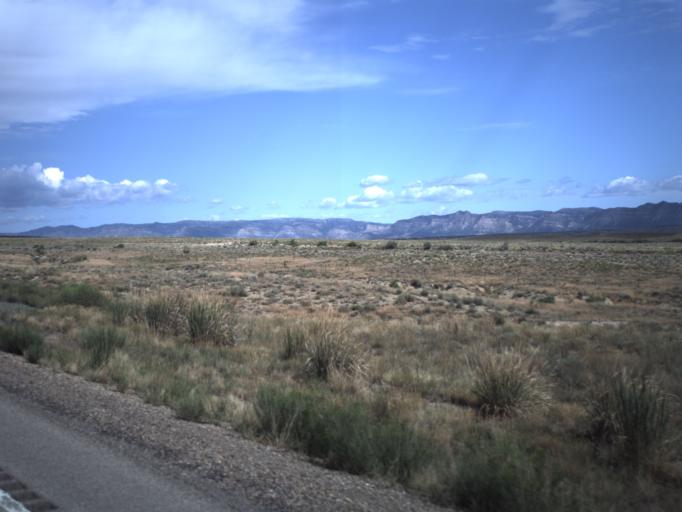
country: US
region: Utah
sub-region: Carbon County
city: Wellington
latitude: 39.5319
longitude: -110.5874
